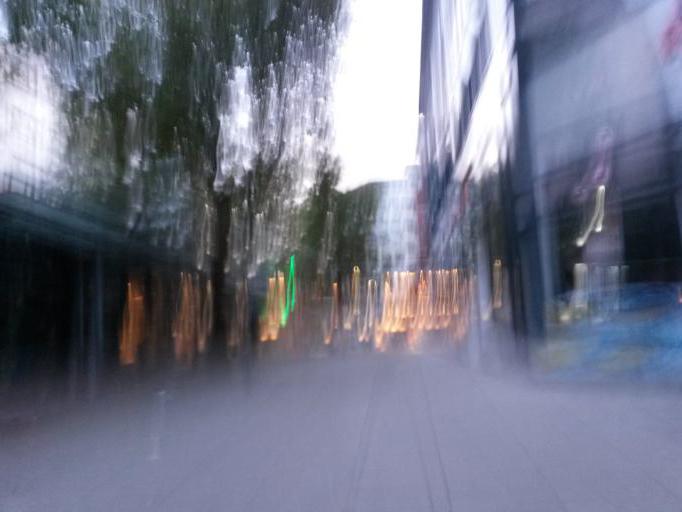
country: DE
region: Bremen
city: Bremen
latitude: 53.0784
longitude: 8.8047
